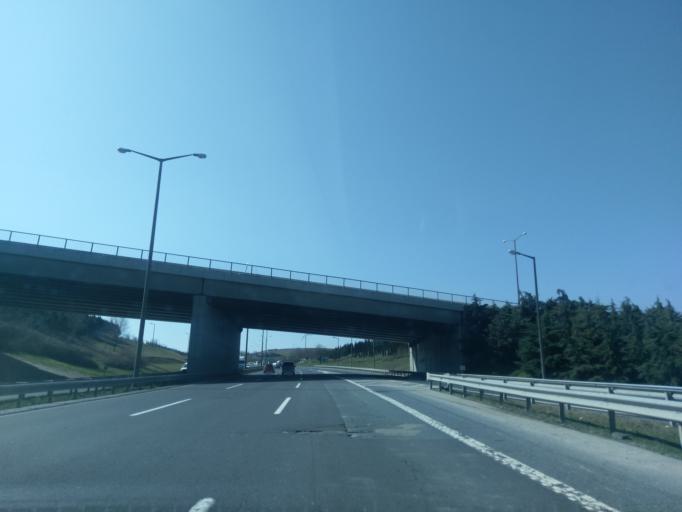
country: TR
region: Istanbul
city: Kumburgaz
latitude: 41.0580
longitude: 28.4654
